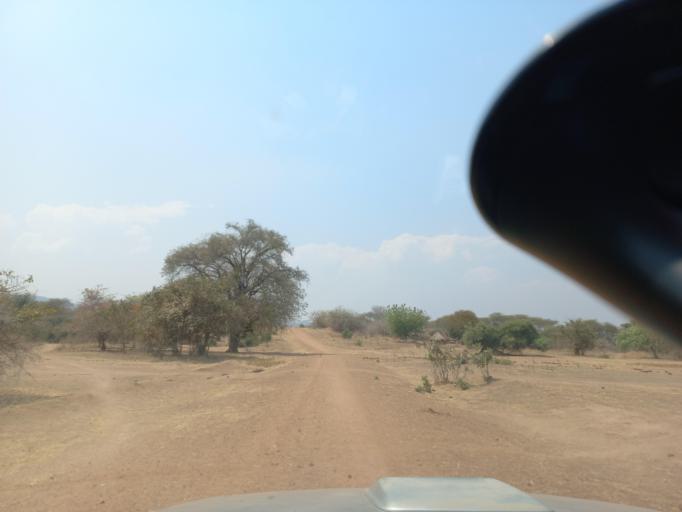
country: ZW
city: Chirundu
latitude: -15.9137
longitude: 28.6866
